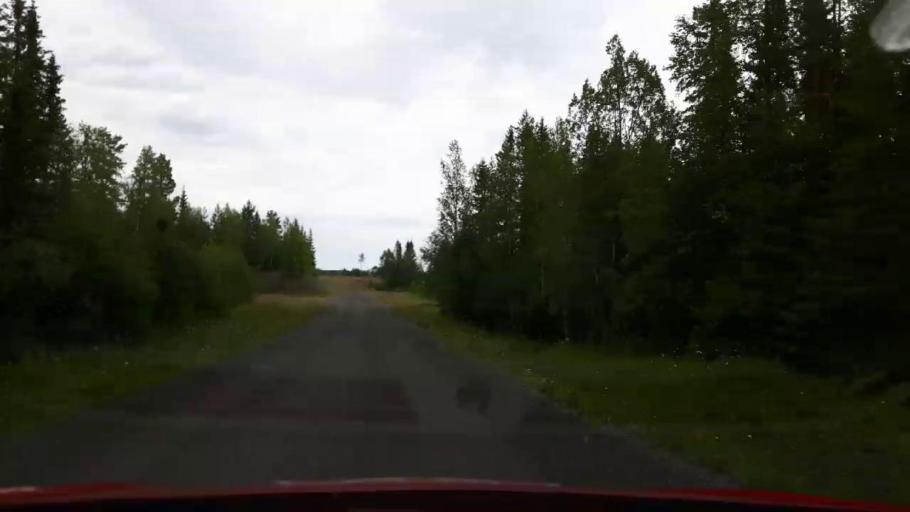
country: SE
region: Jaemtland
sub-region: OEstersunds Kommun
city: Lit
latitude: 63.4090
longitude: 15.2398
